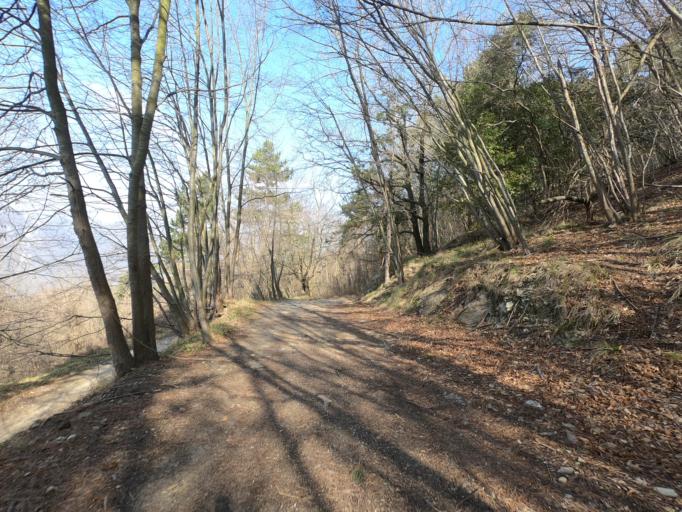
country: IT
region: Liguria
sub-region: Provincia di Savona
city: Castelvecchio di Rocca Barbena
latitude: 44.1270
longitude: 8.1396
